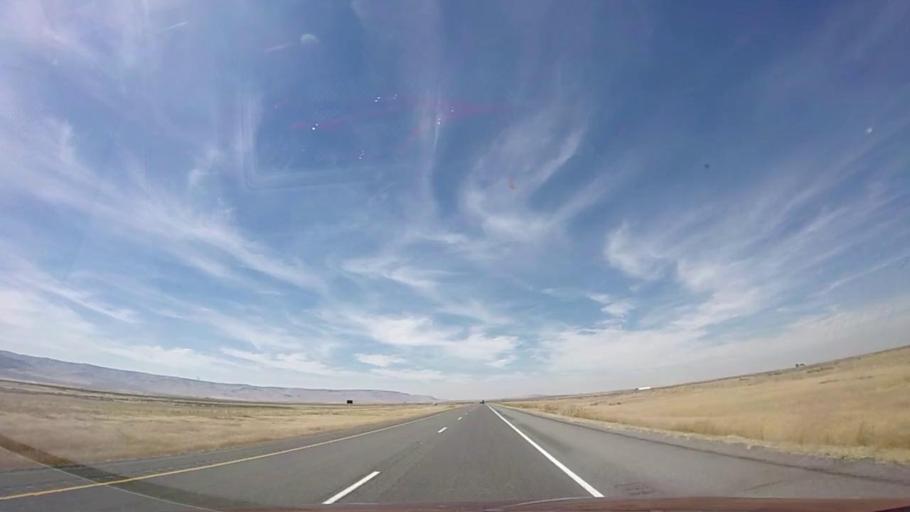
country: US
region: Idaho
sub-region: Minidoka County
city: Rupert
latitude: 42.4026
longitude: -113.3042
